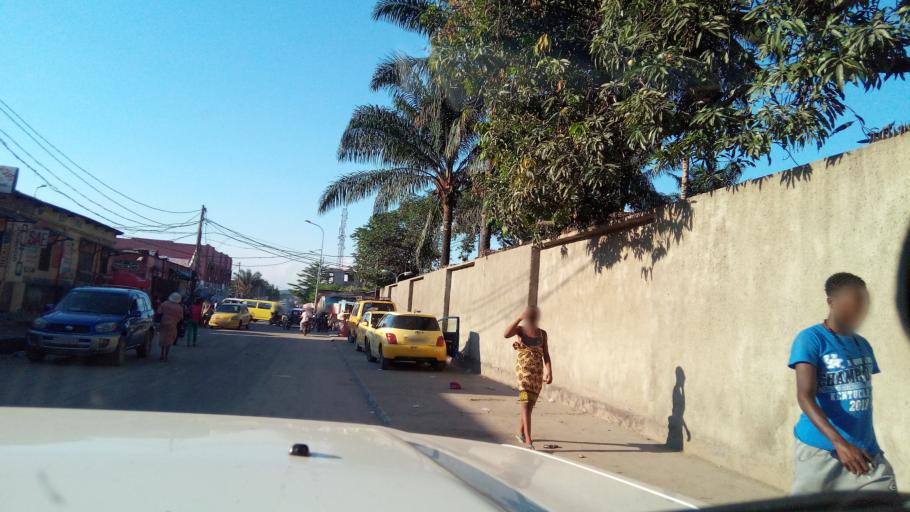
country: CD
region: Kinshasa
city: Kinshasa
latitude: -4.3386
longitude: 15.2667
